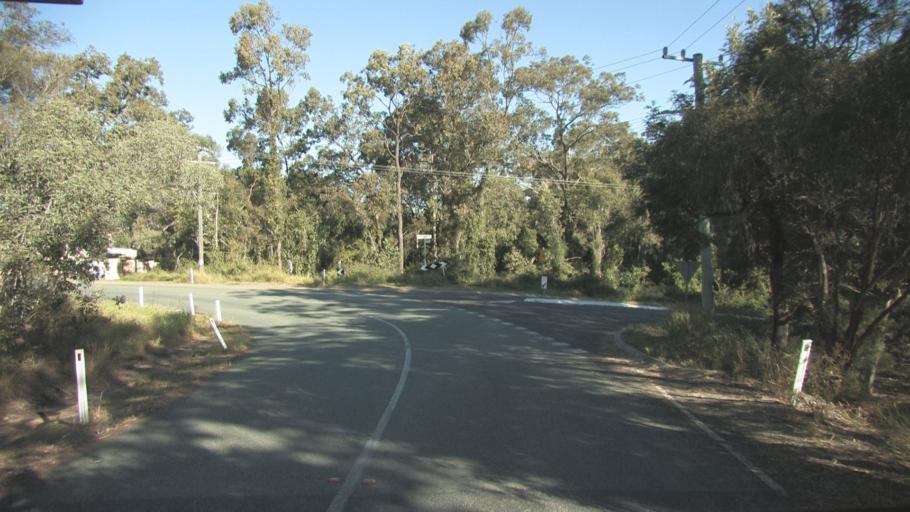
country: AU
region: Queensland
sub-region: Logan
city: Logan Reserve
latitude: -27.7405
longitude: 153.1027
